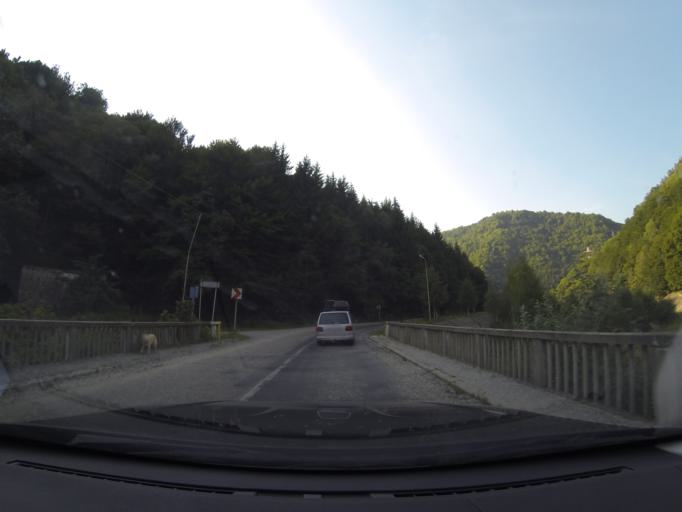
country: RO
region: Arges
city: Poenari
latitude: 45.3449
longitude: 24.6344
